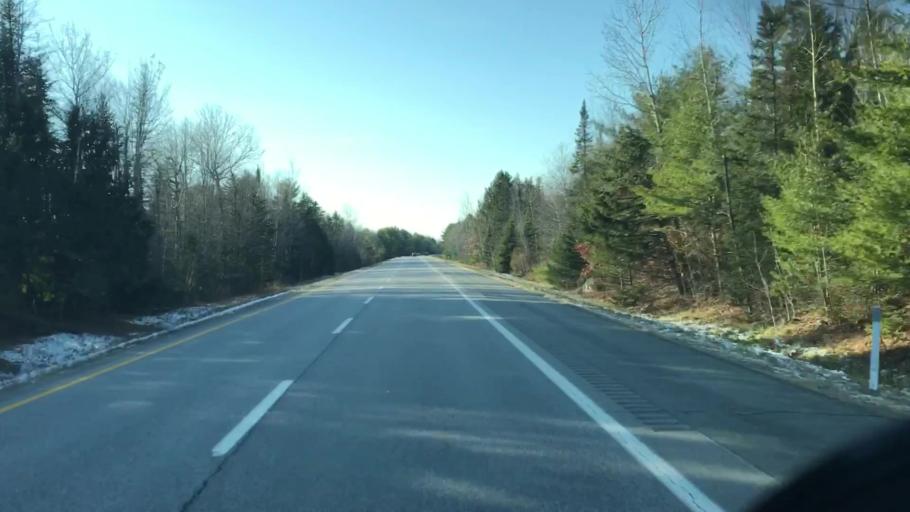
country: US
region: Maine
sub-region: Penobscot County
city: Carmel
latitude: 44.7741
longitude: -69.0233
